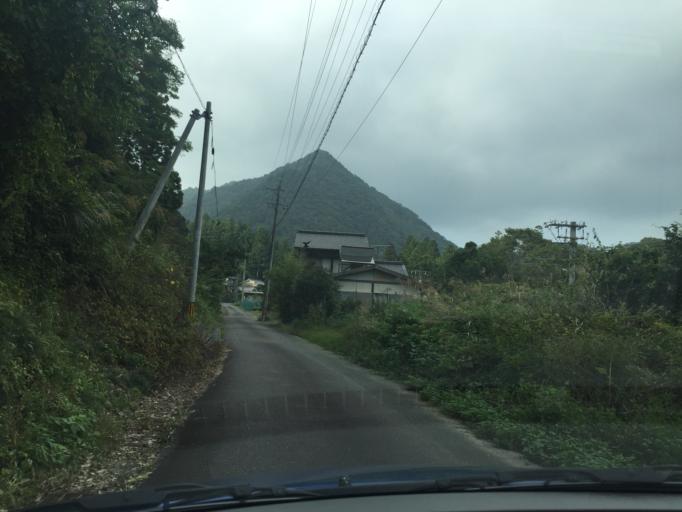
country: JP
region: Aichi
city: Shinshiro
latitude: 34.9765
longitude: 137.6137
